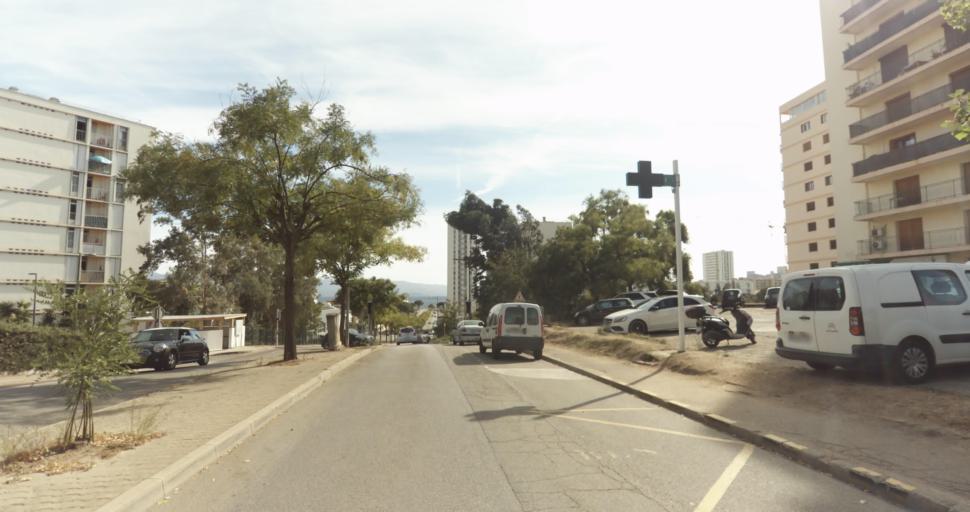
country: FR
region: Corsica
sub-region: Departement de la Corse-du-Sud
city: Ajaccio
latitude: 41.9391
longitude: 8.7508
